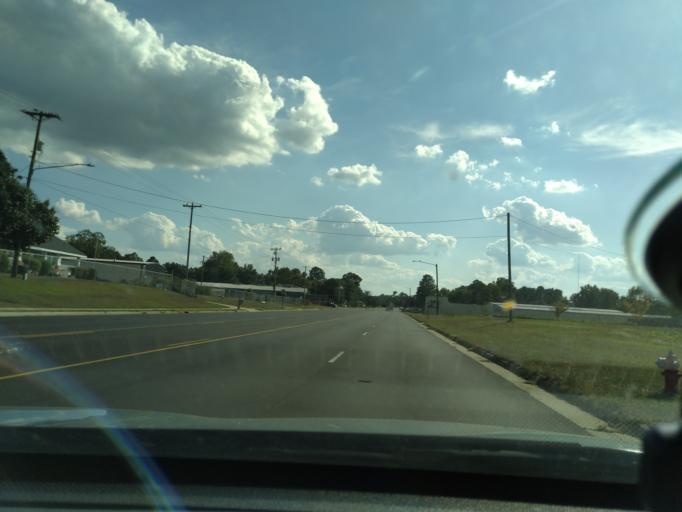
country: US
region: North Carolina
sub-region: Nash County
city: Rocky Mount
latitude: 35.9205
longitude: -77.8251
